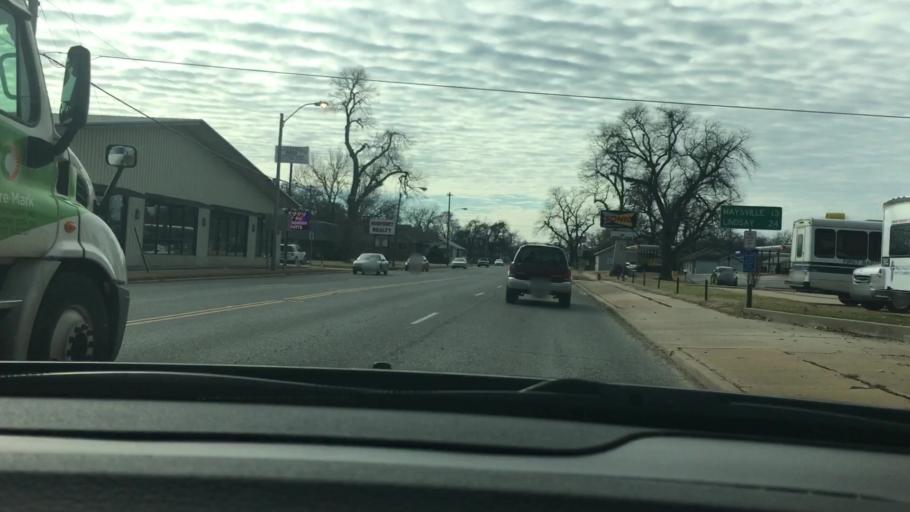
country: US
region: Oklahoma
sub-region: Garvin County
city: Pauls Valley
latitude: 34.7390
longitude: -97.2235
